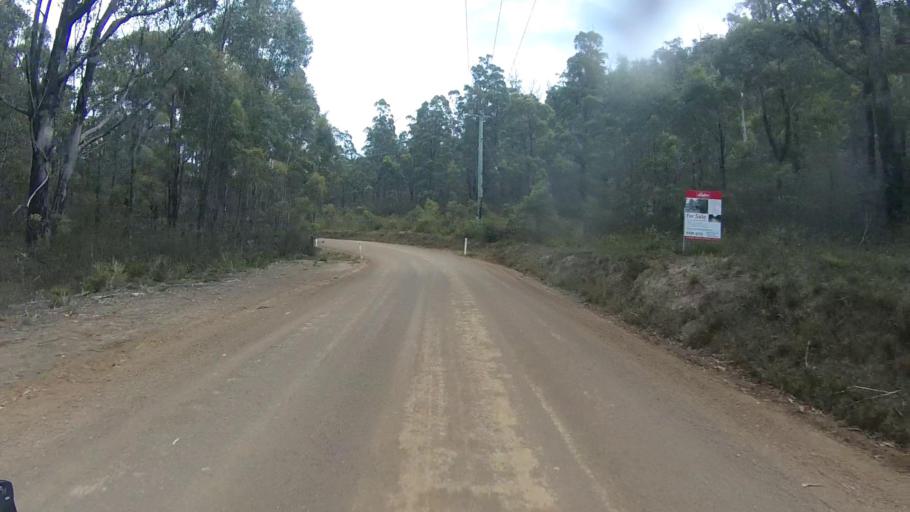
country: AU
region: Tasmania
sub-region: Sorell
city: Sorell
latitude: -42.7501
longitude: 147.7924
